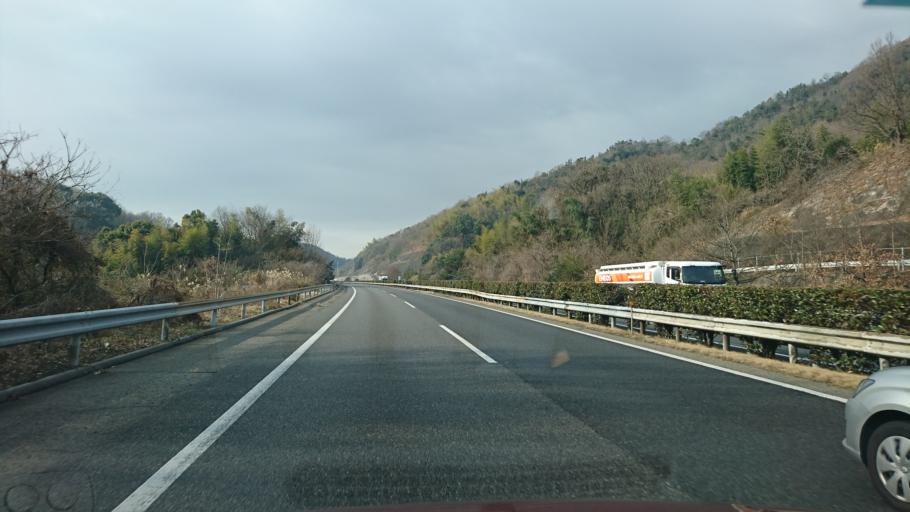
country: JP
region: Okayama
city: Kamogatacho-kamogata
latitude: 34.5664
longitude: 133.6285
